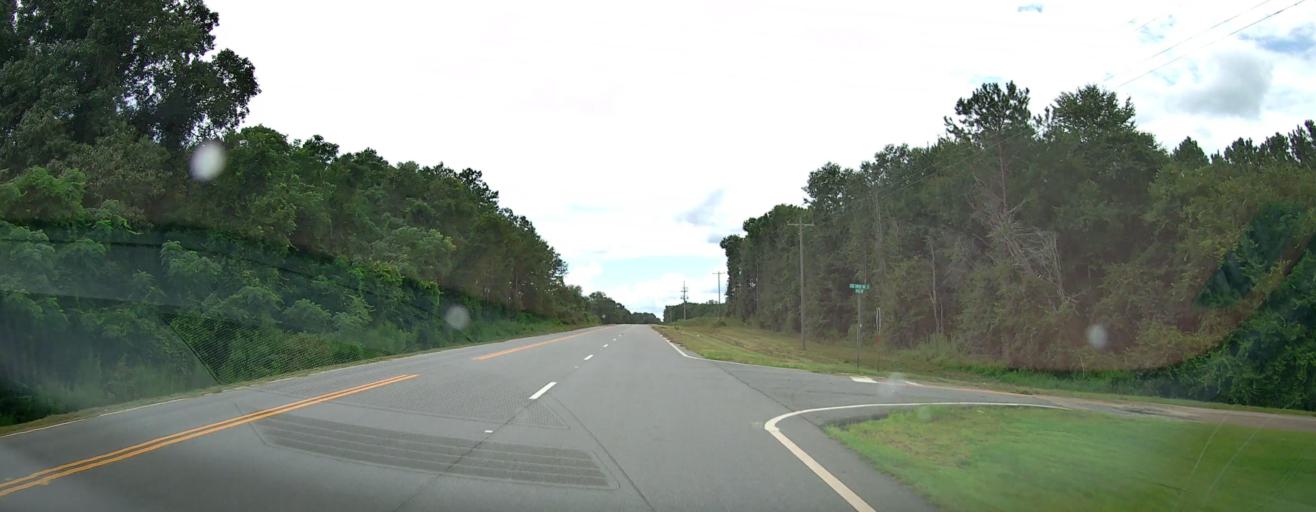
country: US
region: Georgia
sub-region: Schley County
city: Ellaville
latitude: 32.2614
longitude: -84.2095
